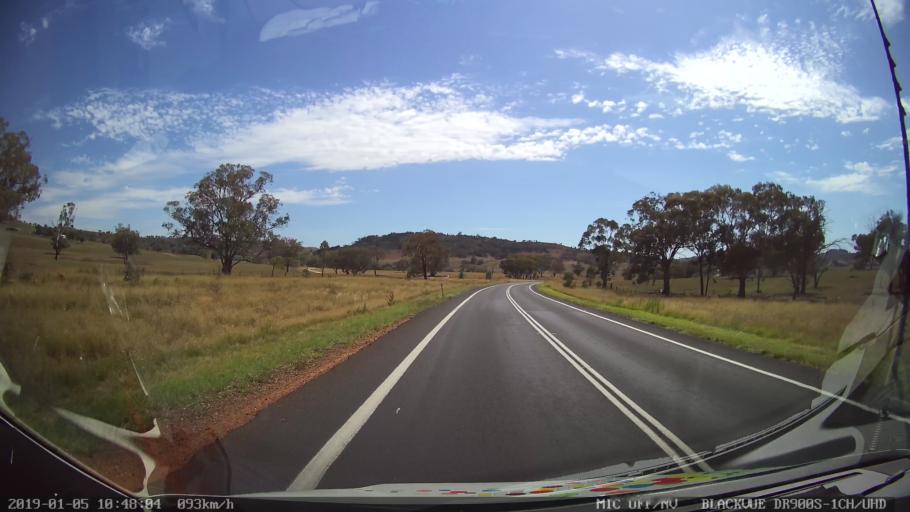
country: AU
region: New South Wales
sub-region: Warrumbungle Shire
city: Coonabarabran
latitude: -31.4393
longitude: 149.0410
